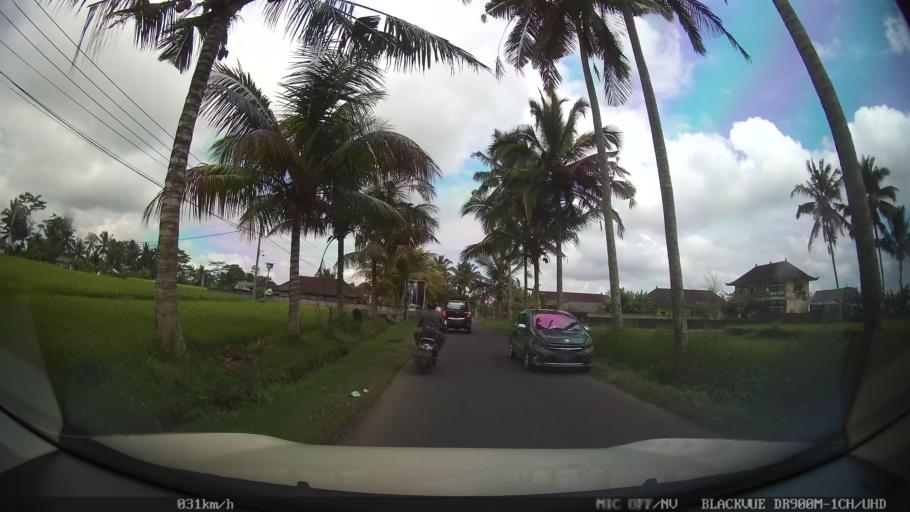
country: ID
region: Bali
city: Bangli
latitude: -8.4581
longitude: 115.3831
